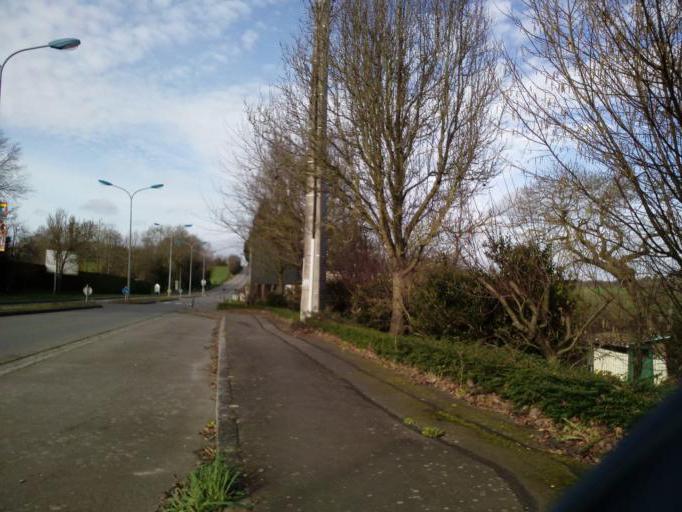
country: FR
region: Brittany
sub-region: Departement d'Ille-et-Vilaine
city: Montgermont
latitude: 48.1565
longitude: -1.7086
